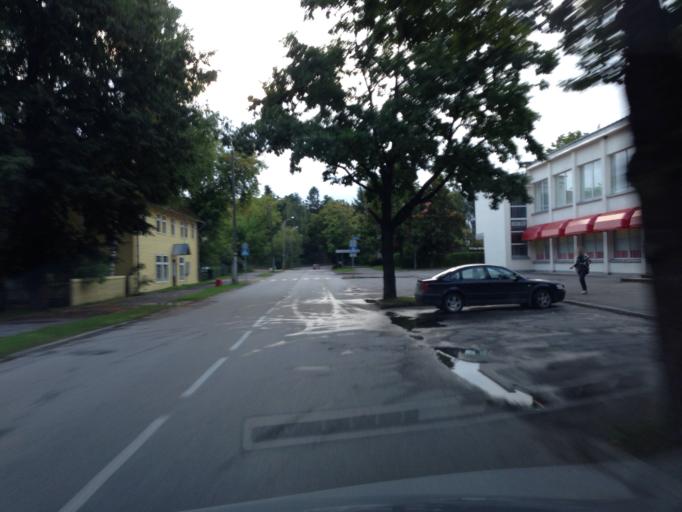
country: EE
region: Tartu
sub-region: Elva linn
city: Elva
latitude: 58.2249
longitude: 26.4205
